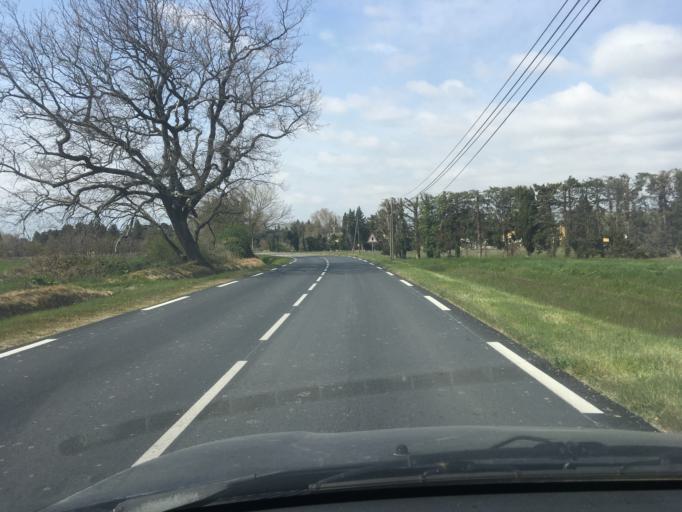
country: FR
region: Provence-Alpes-Cote d'Azur
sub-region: Departement du Vaucluse
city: Aubignan
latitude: 44.0993
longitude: 5.0147
